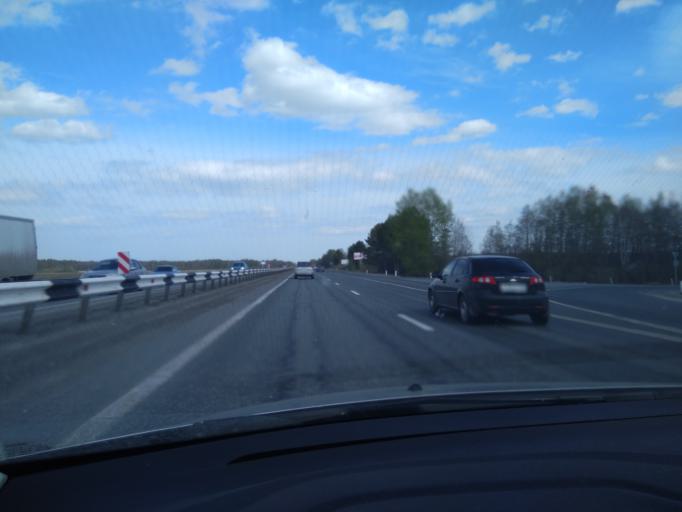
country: RU
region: Tjumen
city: Moskovskiy
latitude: 57.1033
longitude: 65.3296
